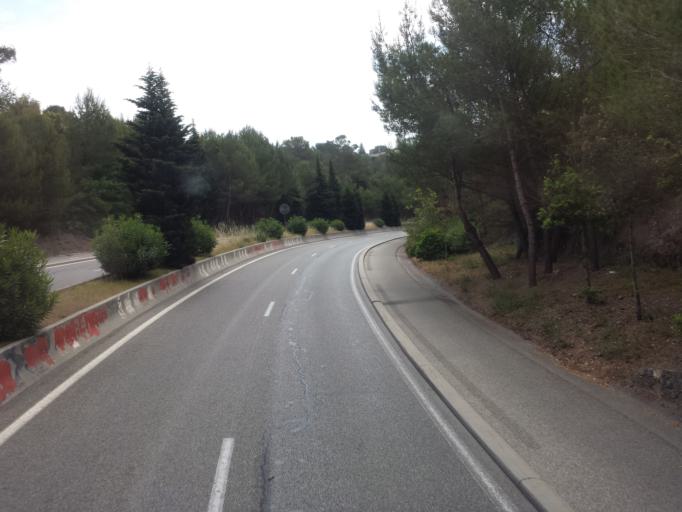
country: FR
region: Provence-Alpes-Cote d'Azur
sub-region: Departement des Alpes-Maritimes
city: Biot
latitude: 43.6112
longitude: 7.0806
